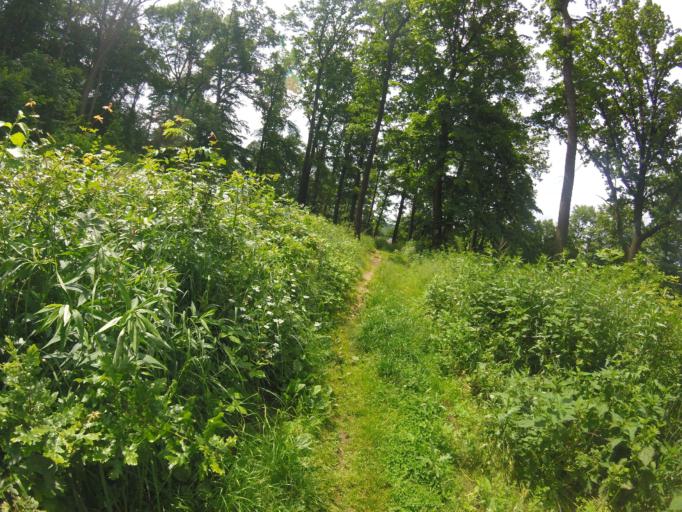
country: HU
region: Veszprem
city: Urkut
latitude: 47.0882
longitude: 17.6490
